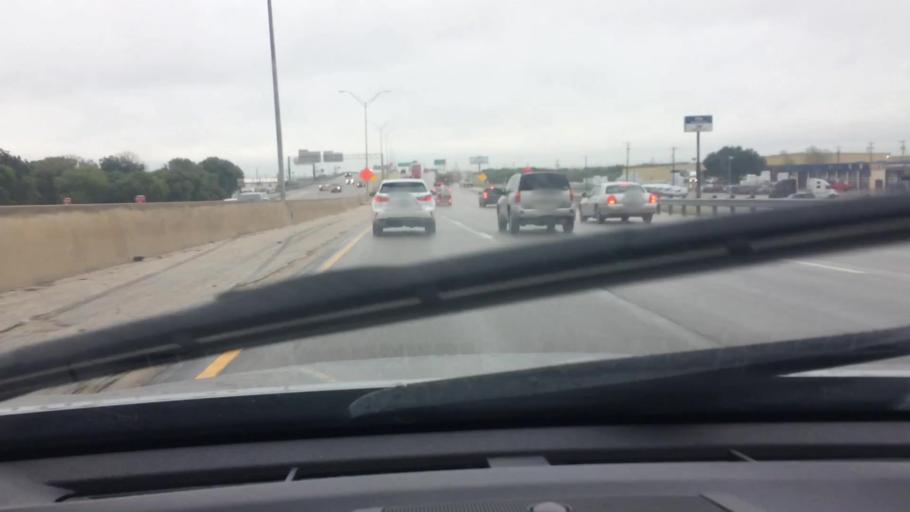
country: US
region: Texas
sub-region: Bexar County
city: Kirby
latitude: 29.4319
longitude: -98.4046
